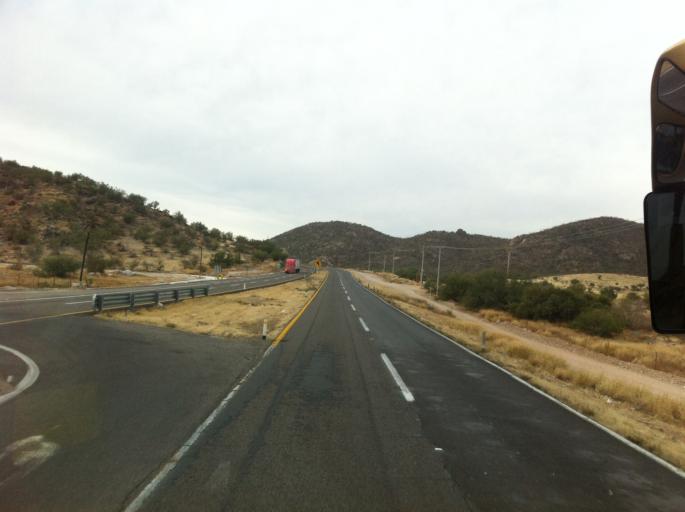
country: MX
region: Sonora
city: Hermosillo
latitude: 28.9976
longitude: -110.9702
